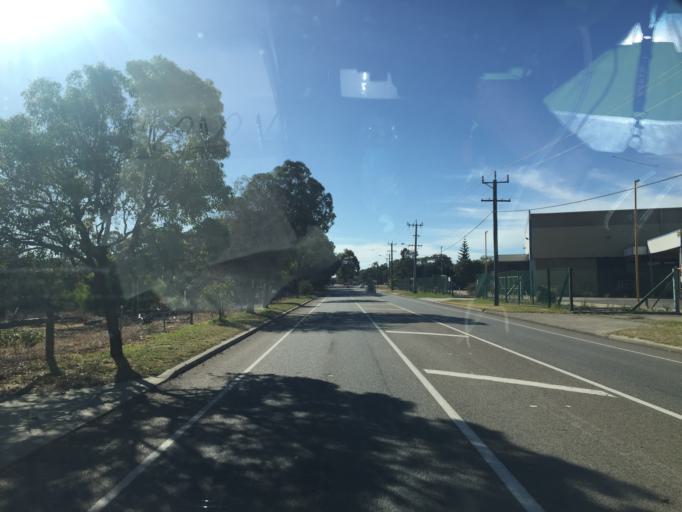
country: AU
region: Western Australia
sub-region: Canning
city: East Cannington
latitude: -32.0009
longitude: 115.9655
